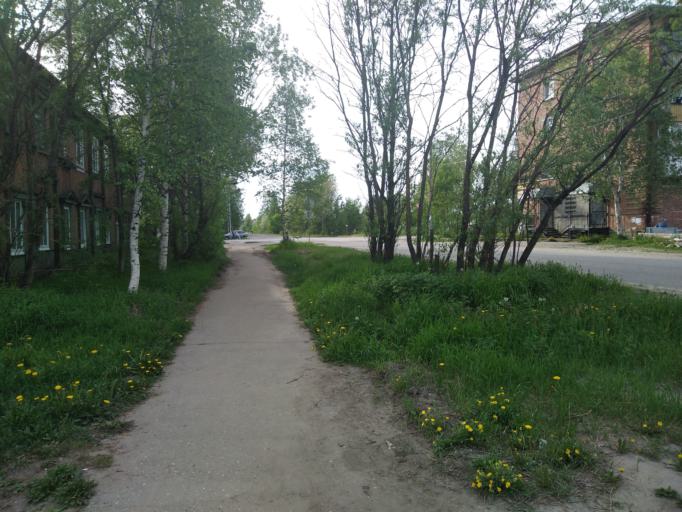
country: RU
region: Komi Republic
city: Pechora
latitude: 65.1462
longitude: 57.2222
